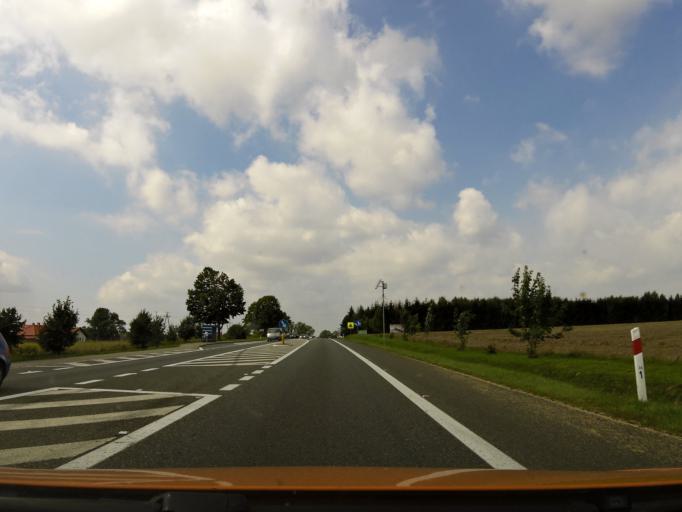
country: PL
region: West Pomeranian Voivodeship
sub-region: Powiat goleniowski
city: Osina
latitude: 53.6330
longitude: 15.0176
